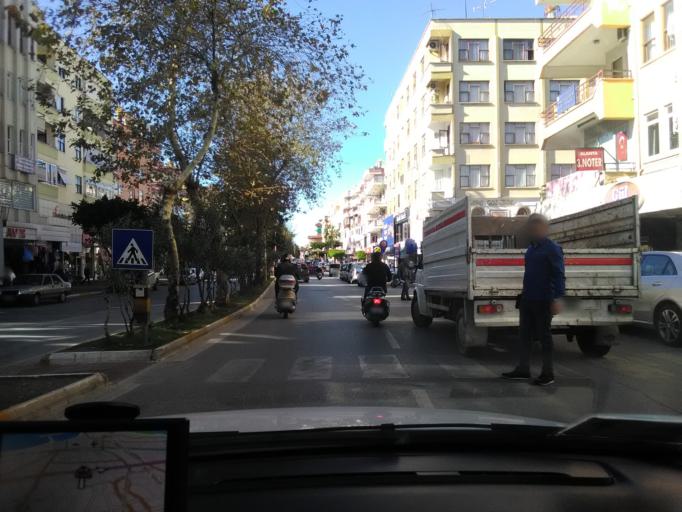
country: TR
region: Antalya
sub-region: Alanya
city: Alanya
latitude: 36.5474
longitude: 31.9998
